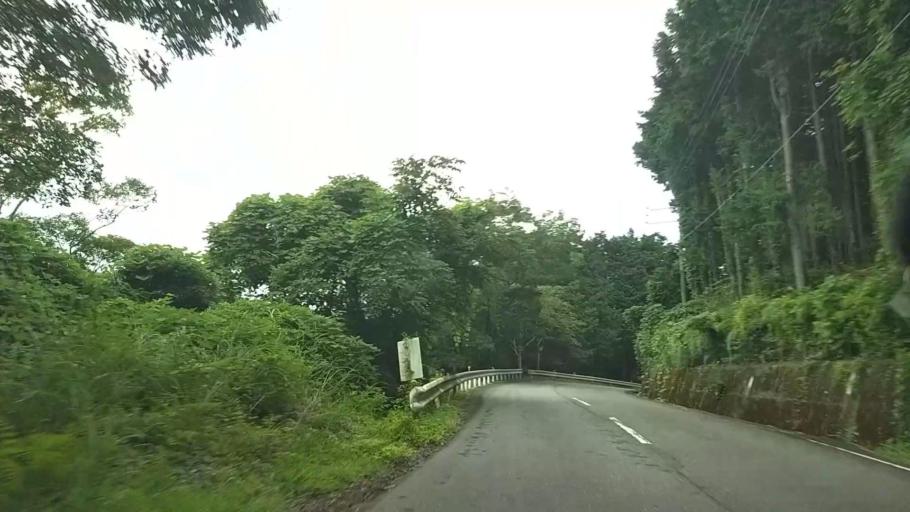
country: JP
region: Shizuoka
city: Fujinomiya
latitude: 35.2112
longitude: 138.5413
